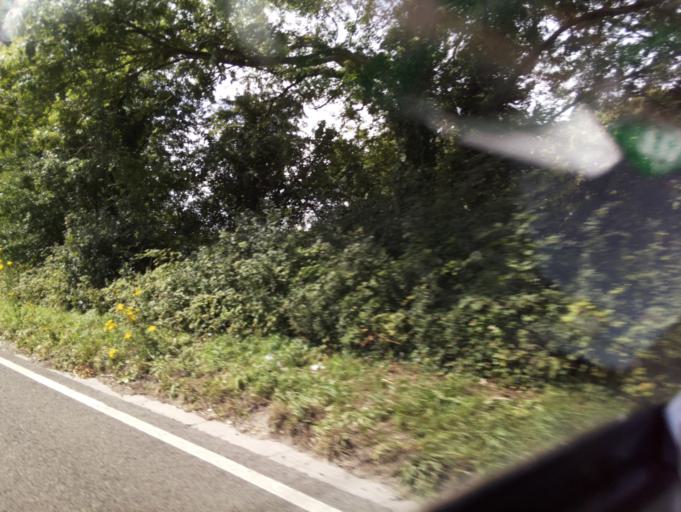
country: GB
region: England
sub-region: Dorset
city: Dorchester
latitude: 50.7438
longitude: -2.4974
